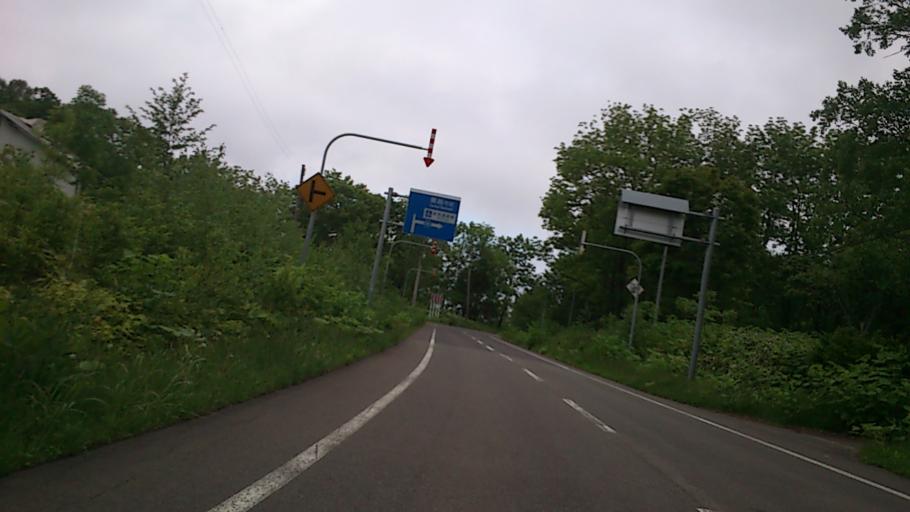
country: JP
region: Hokkaido
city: Niseko Town
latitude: 42.8533
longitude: 140.5706
